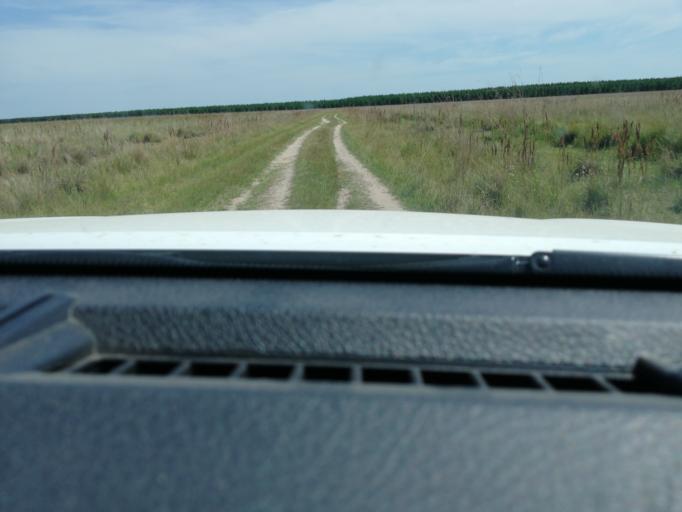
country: AR
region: Corrientes
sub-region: Departamento de San Miguel
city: San Miguel
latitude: -28.0471
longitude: -57.4556
